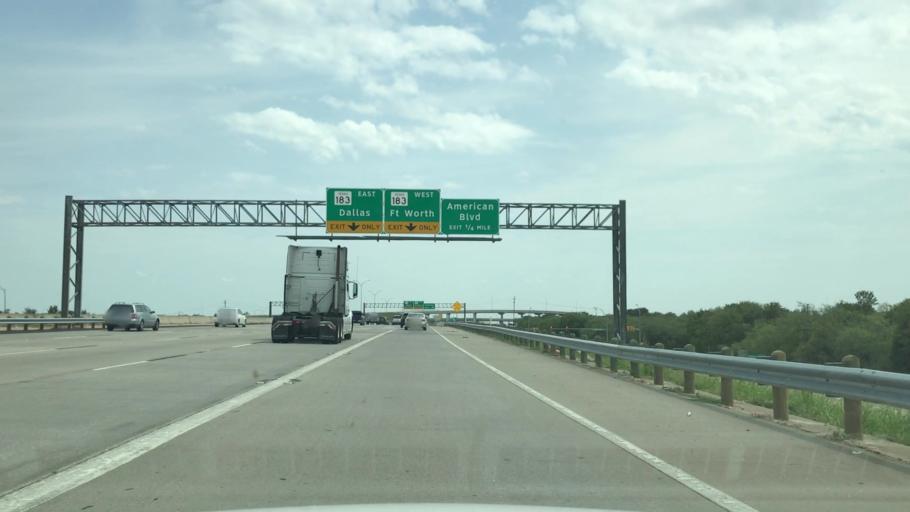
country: US
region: Texas
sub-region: Tarrant County
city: Euless
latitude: 32.8470
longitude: -97.0630
